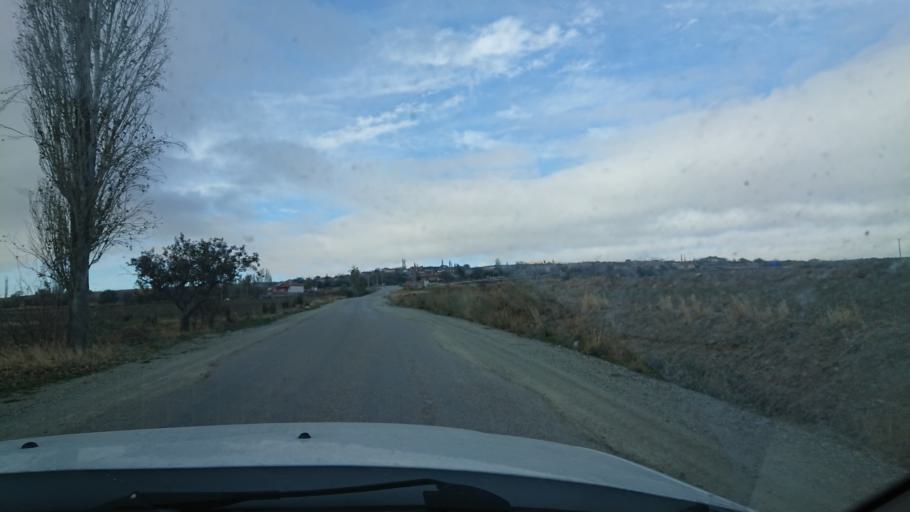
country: TR
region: Aksaray
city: Ortakoy
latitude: 38.7548
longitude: 34.0179
